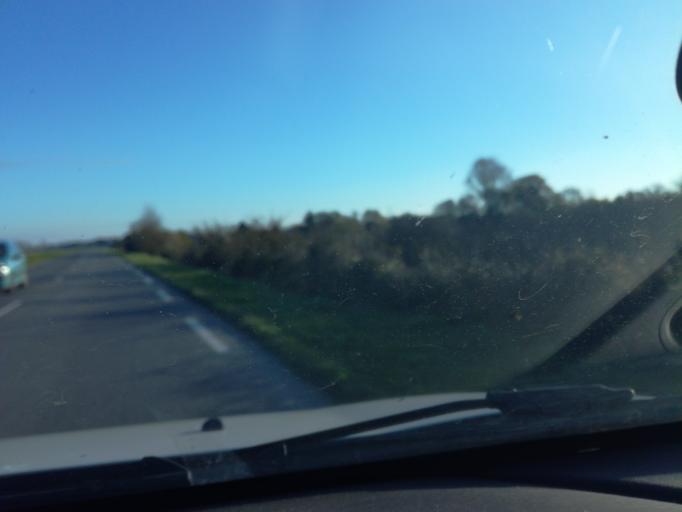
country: FR
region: Brittany
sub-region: Departement d'Ille-et-Vilaine
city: La Fresnais
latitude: 48.6280
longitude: -1.8613
